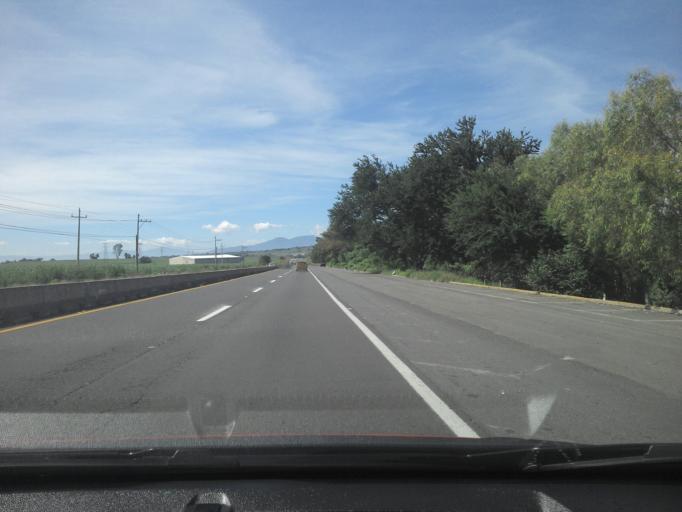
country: MX
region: Jalisco
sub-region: Tala
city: Los Ruisenores
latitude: 20.7085
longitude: -103.6723
